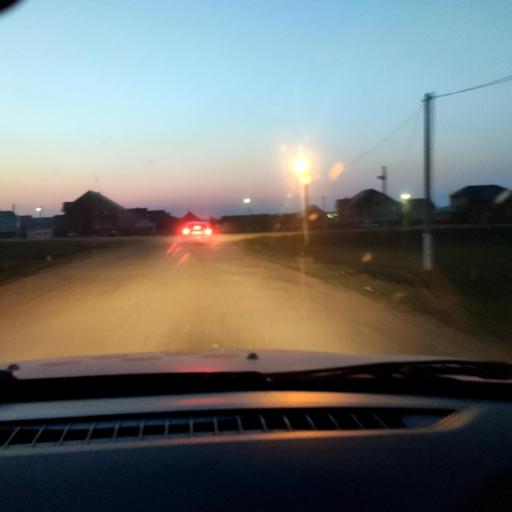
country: RU
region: Bashkortostan
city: Karmaskaly
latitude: 54.3541
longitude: 56.1437
